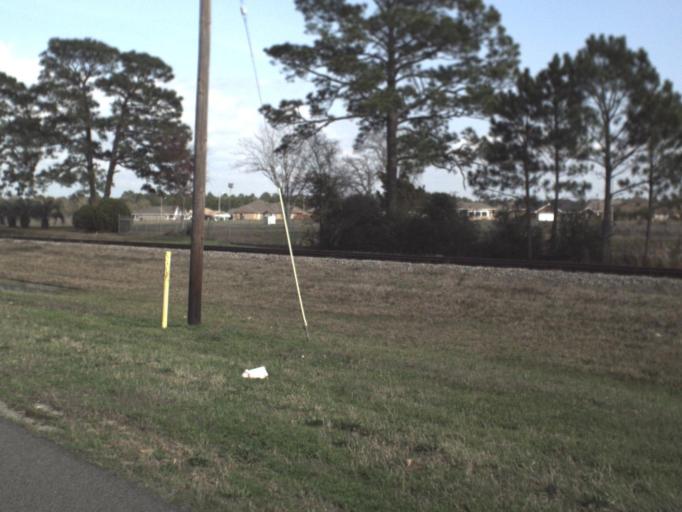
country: US
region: Florida
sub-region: Bay County
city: Hiland Park
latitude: 30.2260
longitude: -85.5892
